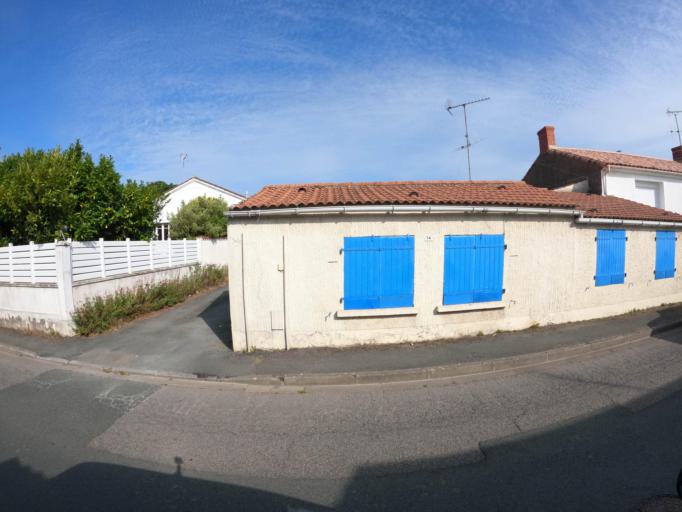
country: FR
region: Pays de la Loire
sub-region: Departement de la Vendee
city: Triaize
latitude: 46.3505
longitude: -1.2505
